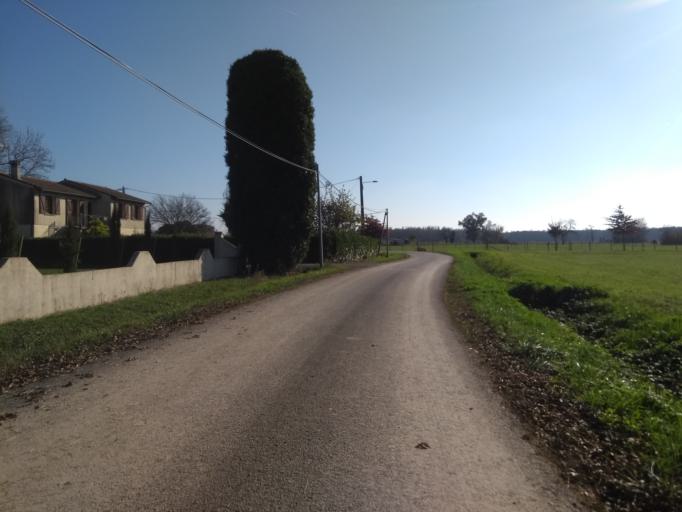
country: FR
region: Aquitaine
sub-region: Departement de la Gironde
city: Cambes
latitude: 44.7239
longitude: -0.4618
